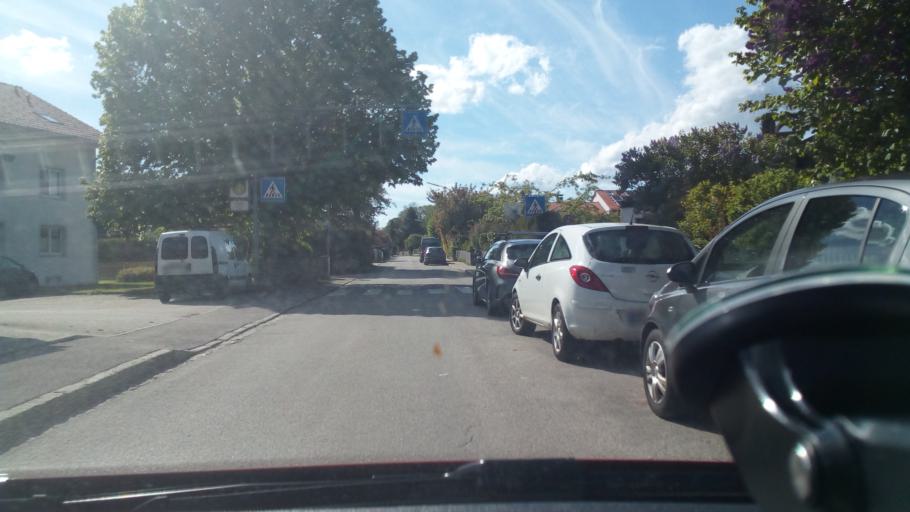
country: DE
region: Bavaria
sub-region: Upper Bavaria
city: Holzkirchen
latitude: 47.8801
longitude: 11.6894
